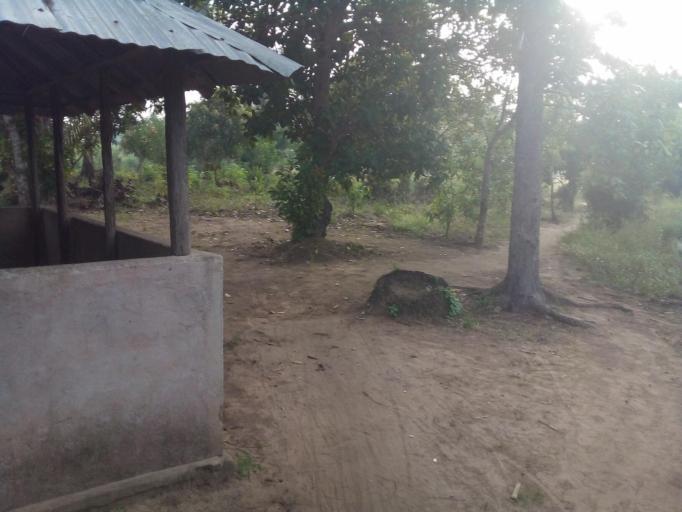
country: MZ
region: Zambezia
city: Quelimane
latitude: -17.5857
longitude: 36.6877
